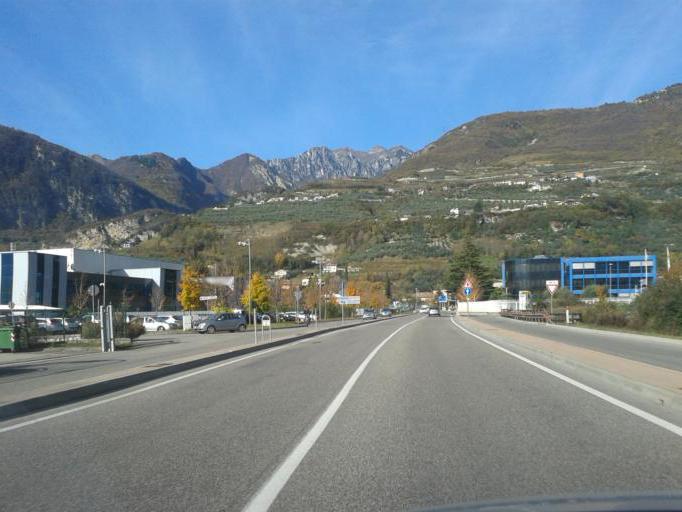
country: IT
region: Trentino-Alto Adige
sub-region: Provincia di Trento
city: Arco
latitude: 45.9108
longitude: 10.8613
